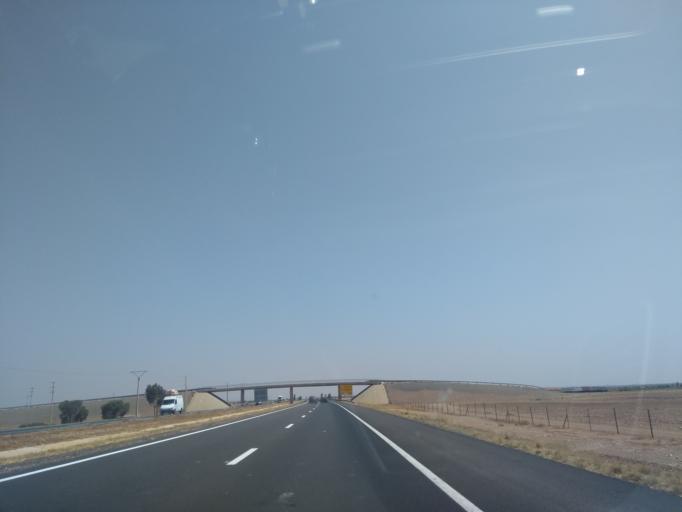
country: MA
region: Marrakech-Tensift-Al Haouz
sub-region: Kelaa-Des-Sraghna
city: Sidi Bou Othmane
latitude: 31.9341
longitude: -8.0178
